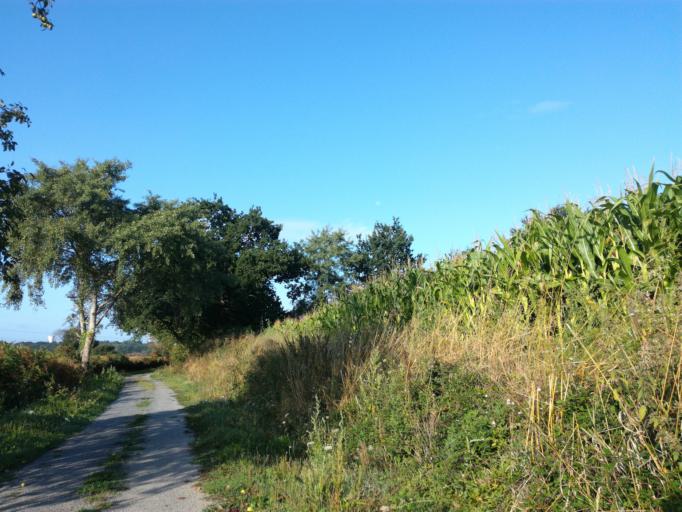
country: FR
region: Brittany
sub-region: Departement d'Ille-et-Vilaine
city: Fouillard
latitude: 48.1485
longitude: -1.5892
